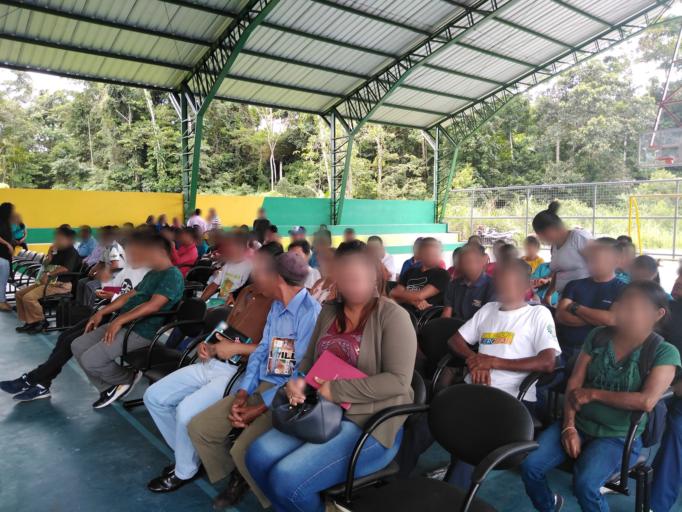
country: EC
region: Napo
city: Tena
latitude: -1.0580
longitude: -77.5478
